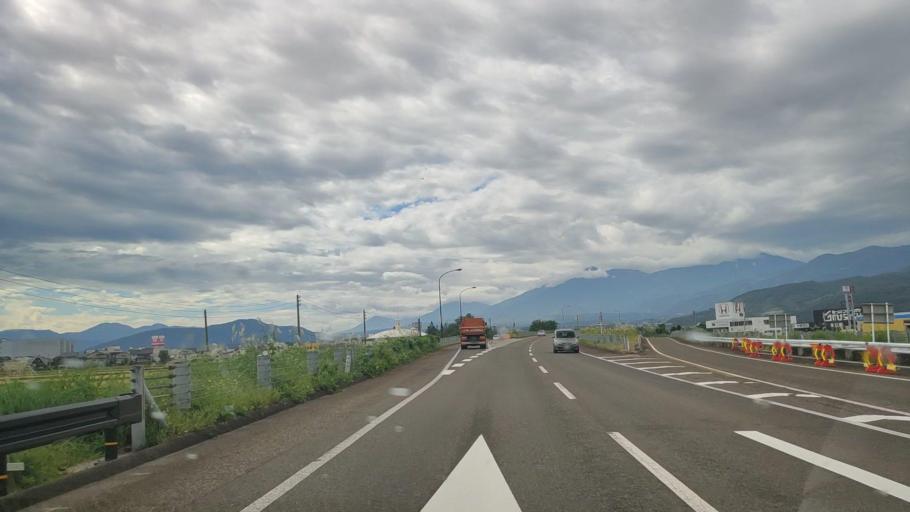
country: JP
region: Niigata
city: Arai
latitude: 37.0621
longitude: 138.2617
